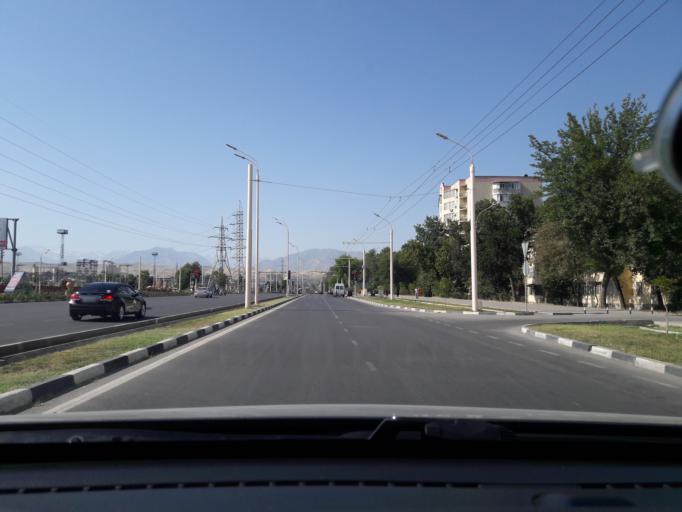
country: TJ
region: Dushanbe
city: Dushanbe
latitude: 38.5551
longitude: 68.7416
